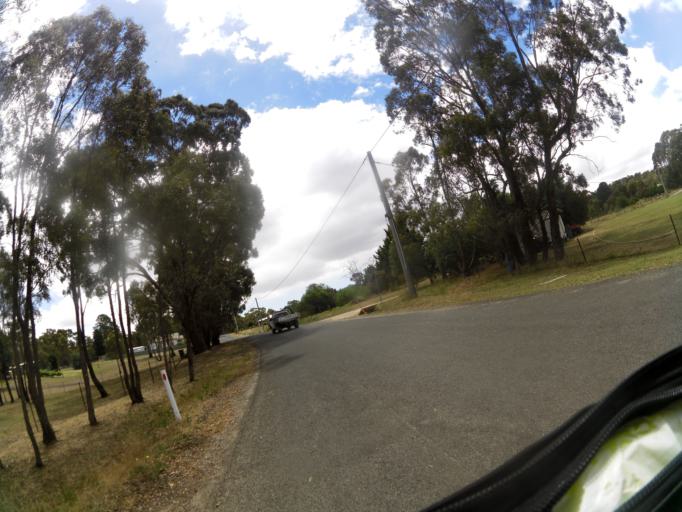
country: AU
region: Victoria
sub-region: Mount Alexander
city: Castlemaine
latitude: -37.0254
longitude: 144.2416
